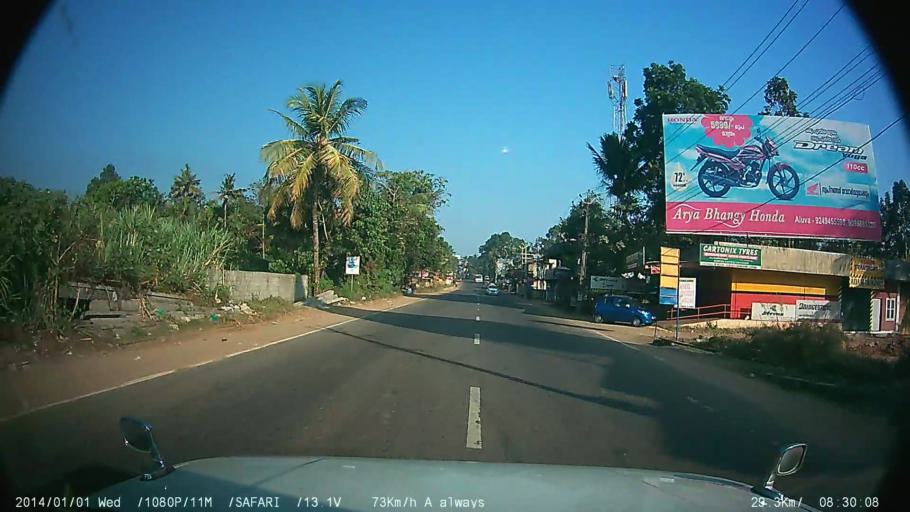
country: IN
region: Kerala
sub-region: Ernakulam
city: Perumbavoor
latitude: 10.1055
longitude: 76.4824
